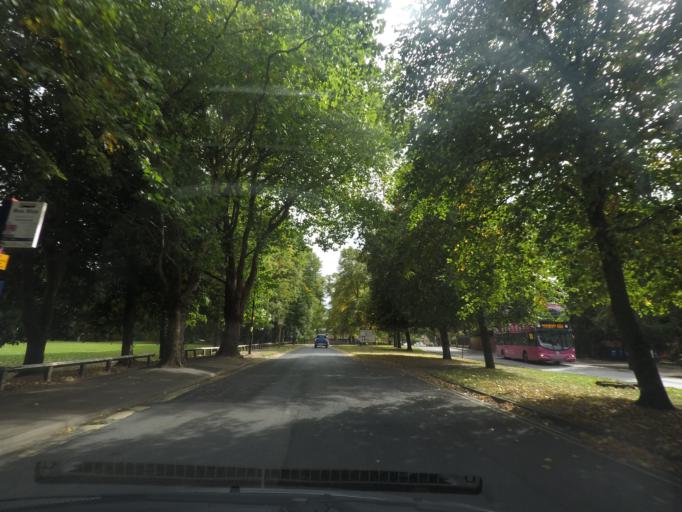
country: GB
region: England
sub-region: City of York
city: Heslington
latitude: 53.9469
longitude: -1.0466
